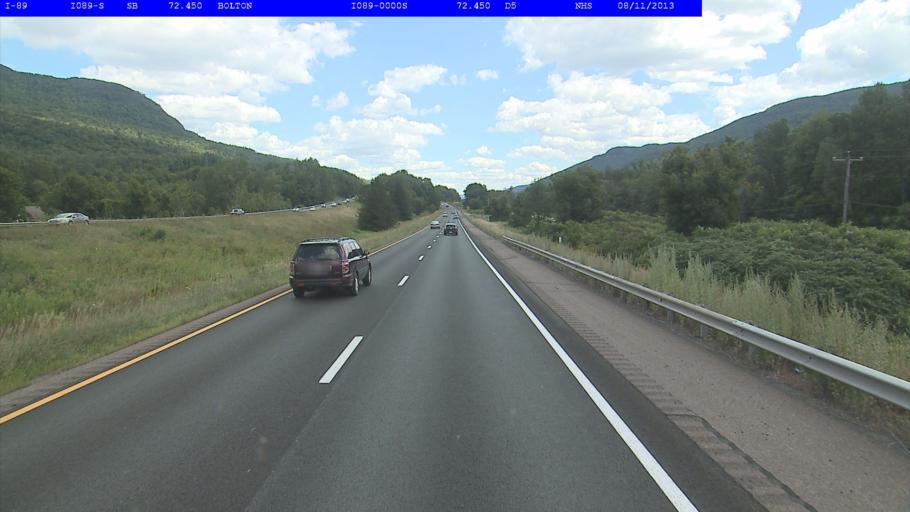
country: US
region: Vermont
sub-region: Chittenden County
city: Jericho
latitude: 44.3804
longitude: -72.9152
